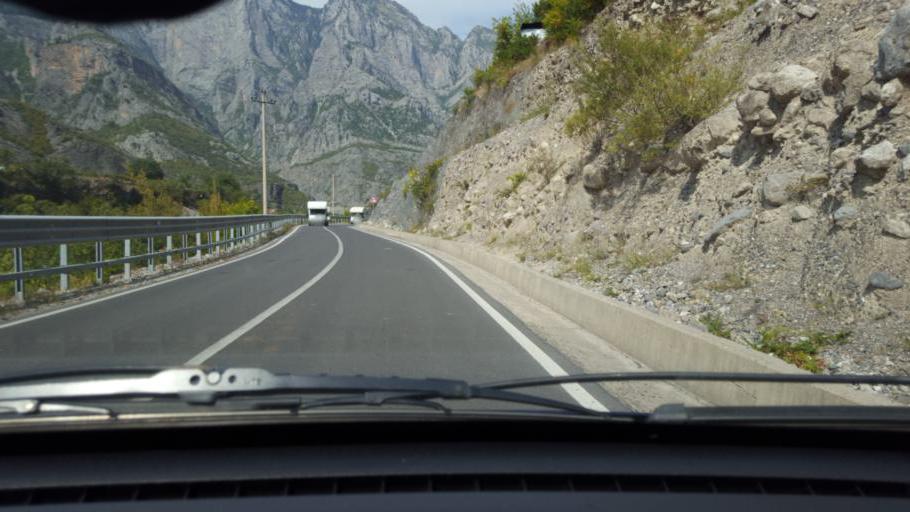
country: AL
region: Shkoder
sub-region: Rrethi i Malesia e Madhe
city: Kastrat
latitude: 42.4555
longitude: 19.5609
